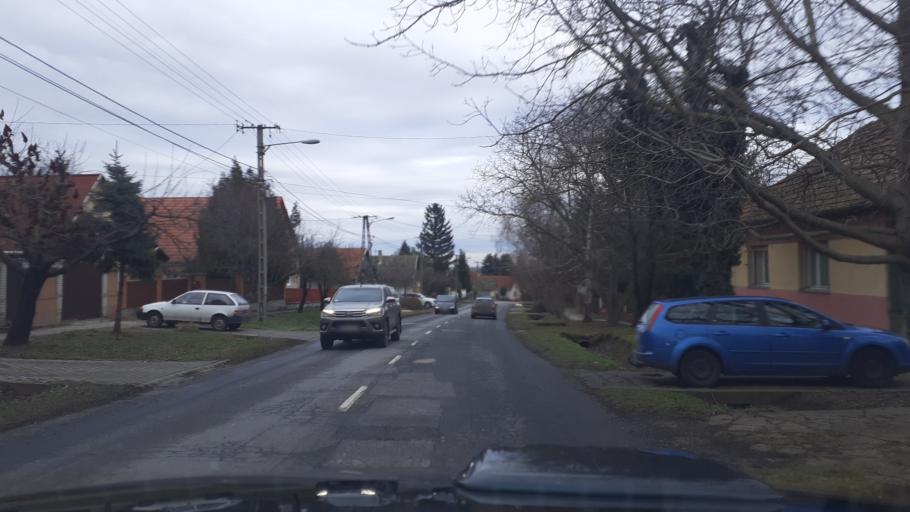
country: HU
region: Fejer
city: dunaujvaros
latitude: 46.9791
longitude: 18.9257
